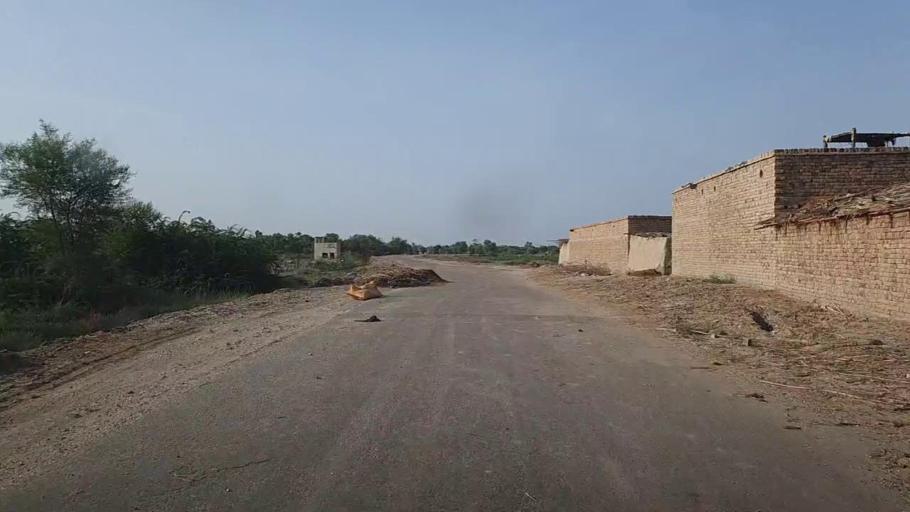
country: PK
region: Sindh
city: Ubauro
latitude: 28.0970
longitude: 69.8456
